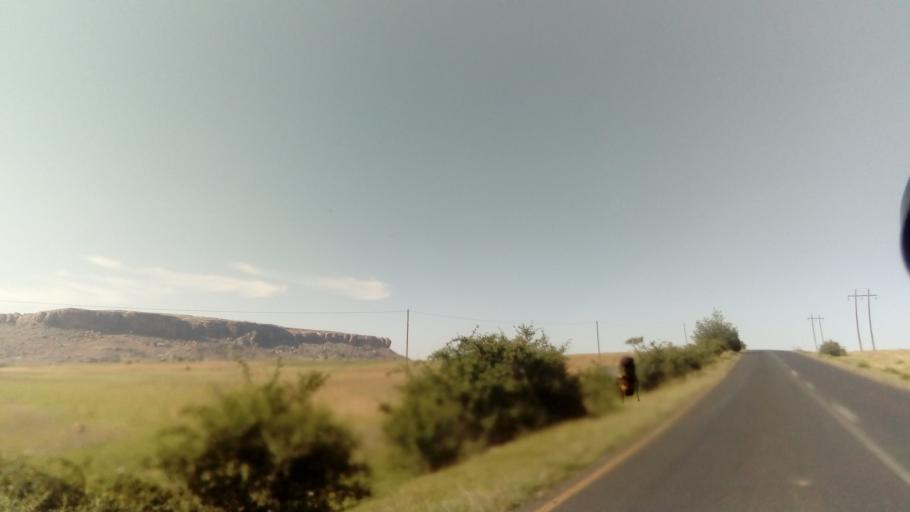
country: LS
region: Berea
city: Teyateyaneng
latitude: -29.1610
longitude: 27.6527
